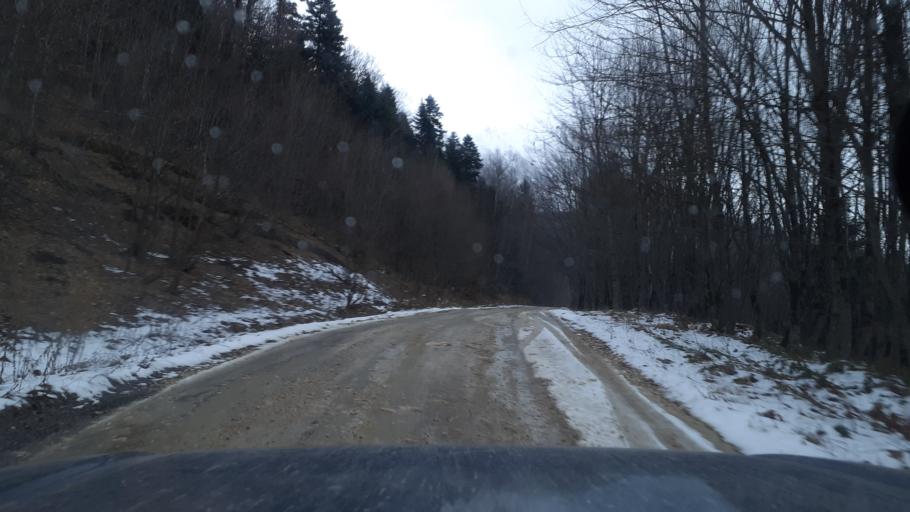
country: RU
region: Krasnodarskiy
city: Neftegorsk
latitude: 44.0788
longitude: 39.7991
